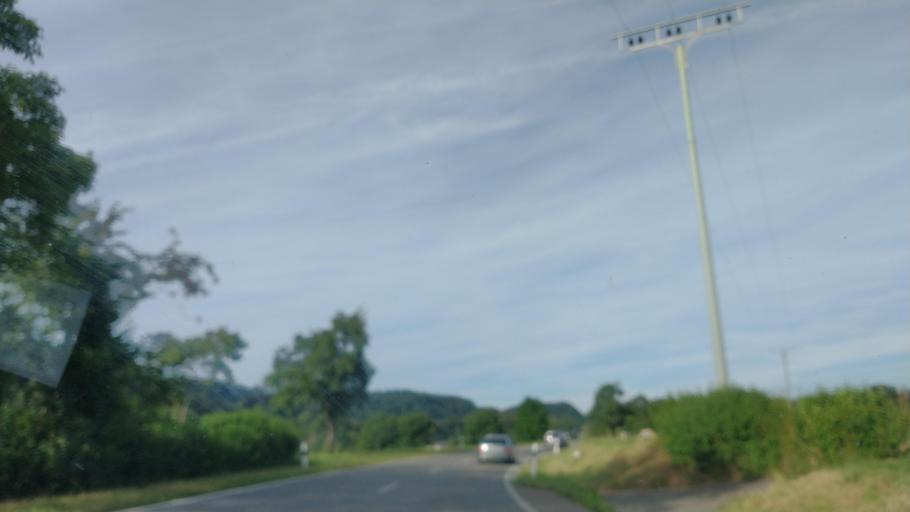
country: DE
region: Baden-Wuerttemberg
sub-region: Tuebingen Region
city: Kressbronn am Bodensee
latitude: 47.6308
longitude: 9.6187
